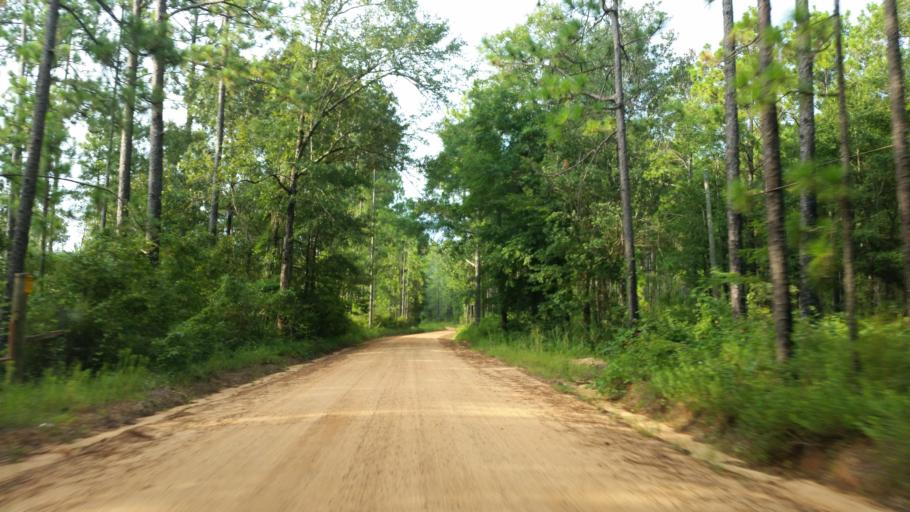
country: US
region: Alabama
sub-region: Escambia County
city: Atmore
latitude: 30.9022
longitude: -87.5827
